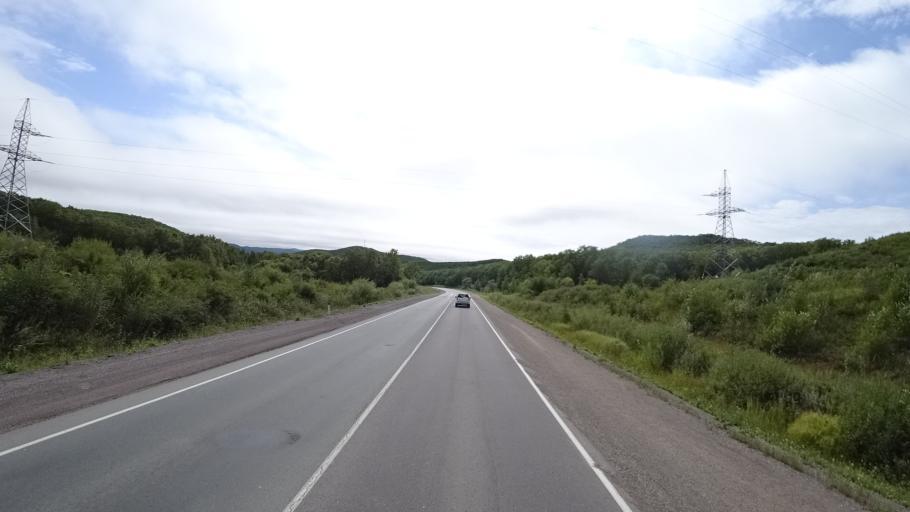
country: RU
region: Primorskiy
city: Lyalichi
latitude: 44.1222
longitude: 132.4213
